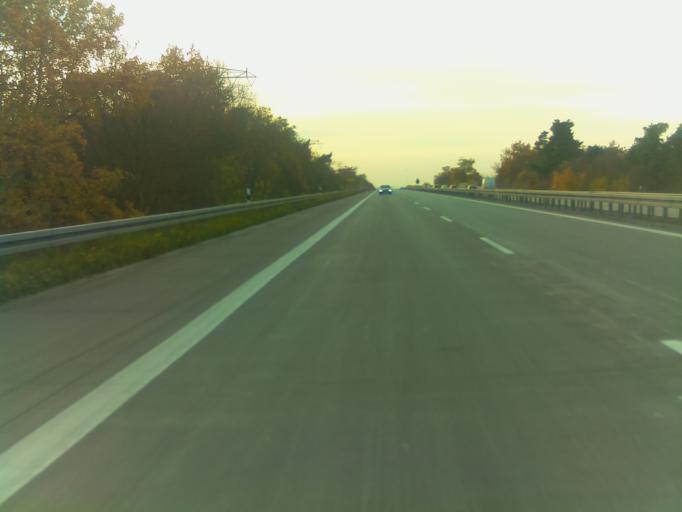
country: DE
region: Hesse
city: Lampertheim
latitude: 49.5544
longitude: 8.4865
